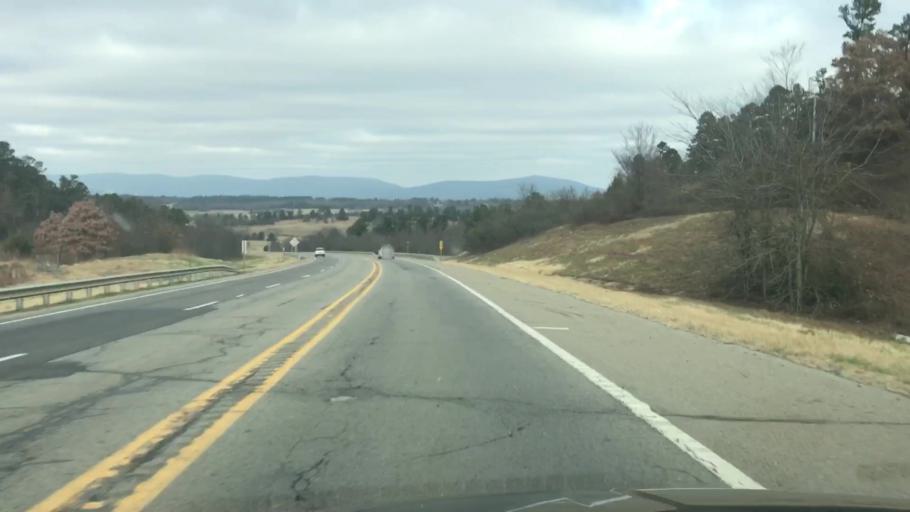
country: US
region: Arkansas
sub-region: Scott County
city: Waldron
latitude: 34.8652
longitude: -94.0746
